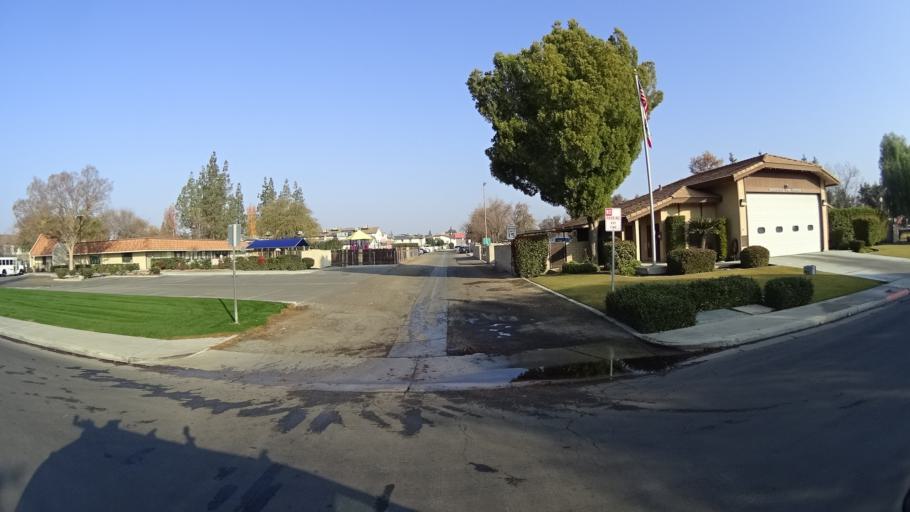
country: US
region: California
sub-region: Kern County
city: Greenacres
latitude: 35.3301
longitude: -119.0912
